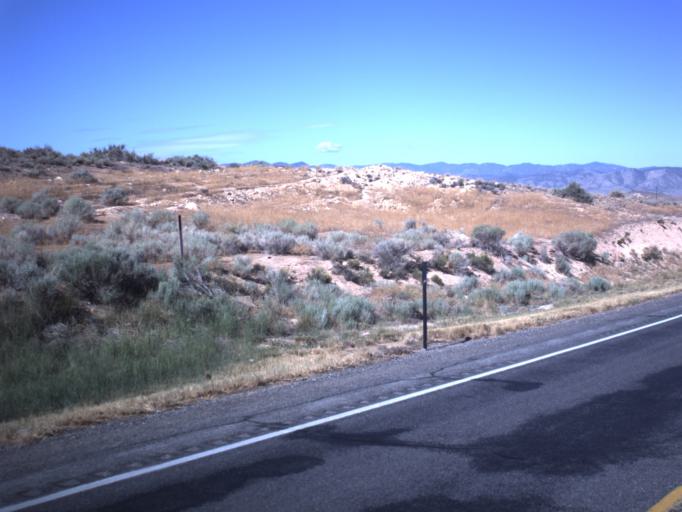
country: US
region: Utah
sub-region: Sanpete County
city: Gunnison
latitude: 39.1613
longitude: -111.7906
